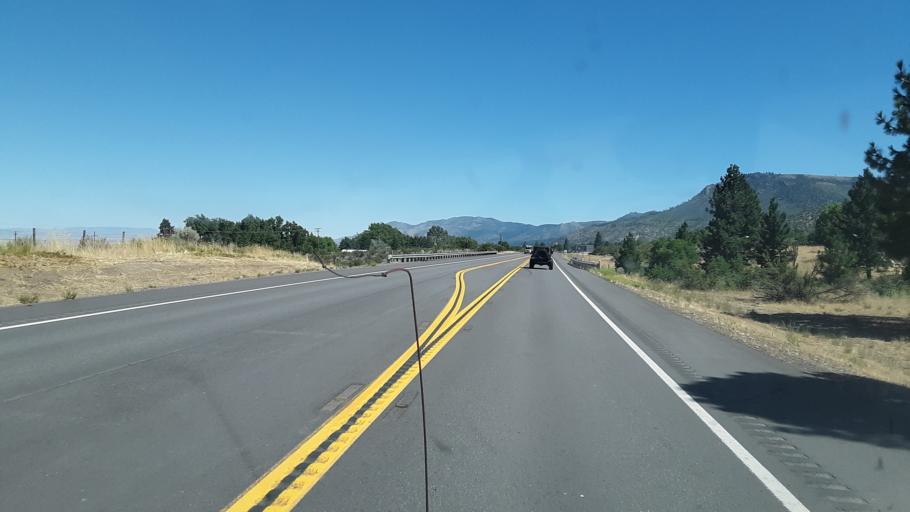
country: US
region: California
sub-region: Lassen County
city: Janesville
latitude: 40.2647
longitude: -120.4731
